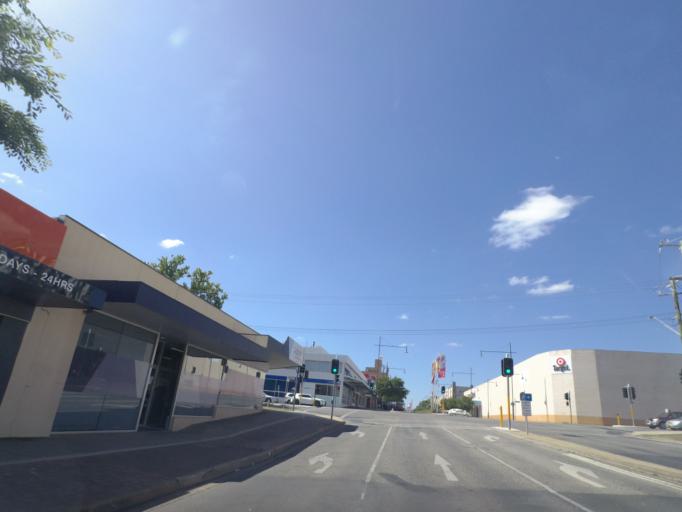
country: AU
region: New South Wales
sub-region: Albury Municipality
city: South Albury
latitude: -36.0831
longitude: 146.9151
